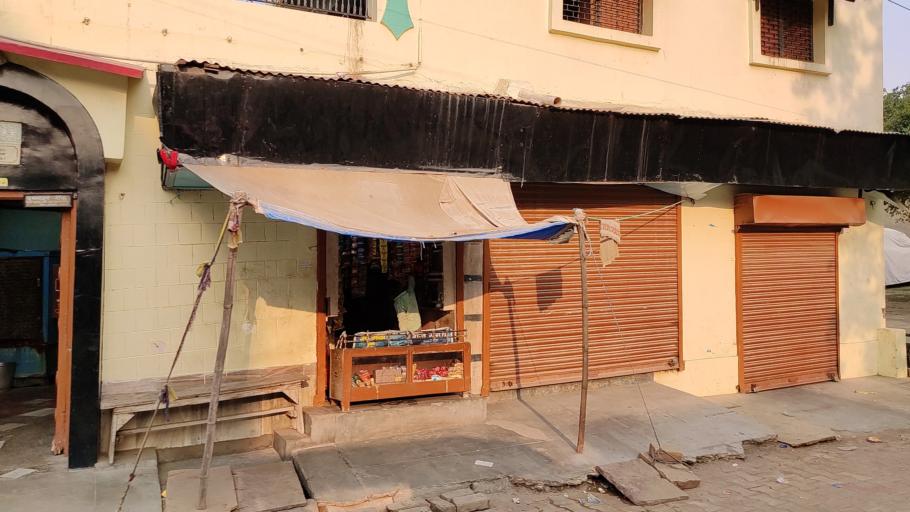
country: IN
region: Uttar Pradesh
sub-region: Mathura
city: Mathura
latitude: 27.5143
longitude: 77.6745
